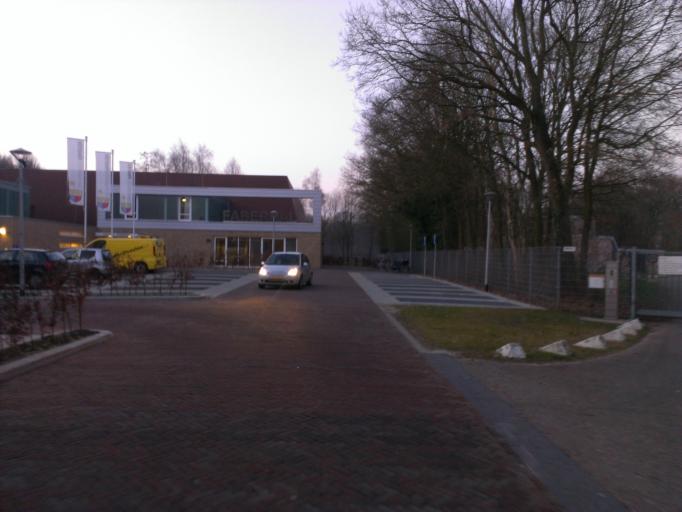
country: NL
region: Gelderland
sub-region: Gemeente Heerde
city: Heerde
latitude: 52.3909
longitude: 6.0531
